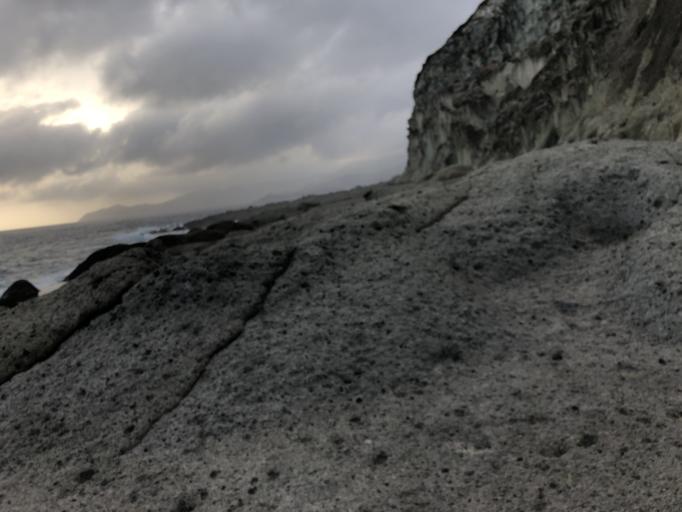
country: IT
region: Sardinia
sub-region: Provincia di Oristano
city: Bosa
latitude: 40.2993
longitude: 8.4664
